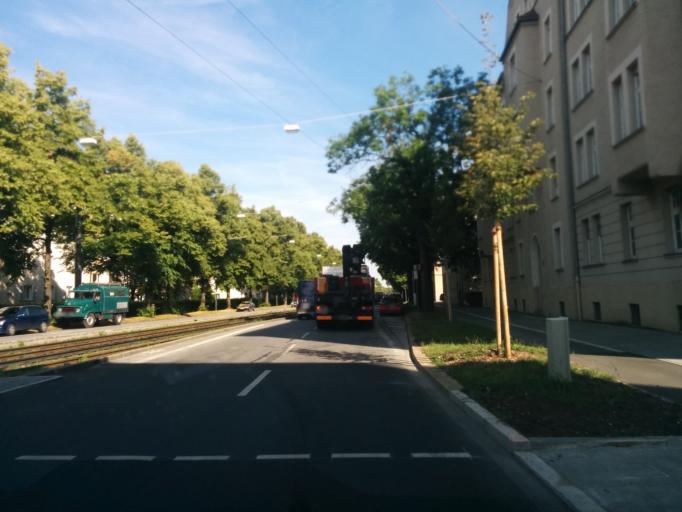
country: DE
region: Bavaria
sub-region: Upper Bavaria
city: Munich
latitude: 48.1554
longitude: 11.5524
